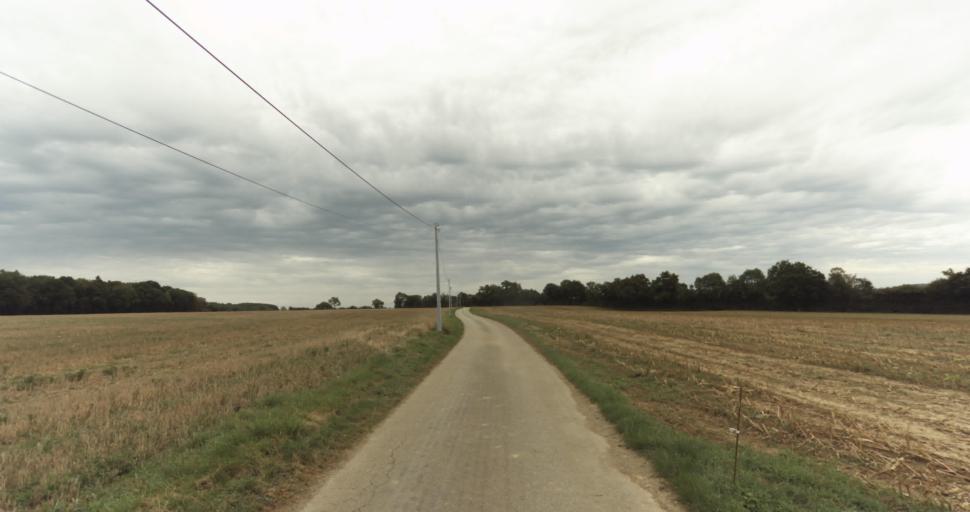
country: FR
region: Lower Normandy
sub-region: Departement de l'Orne
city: Gace
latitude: 48.6845
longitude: 0.2851
